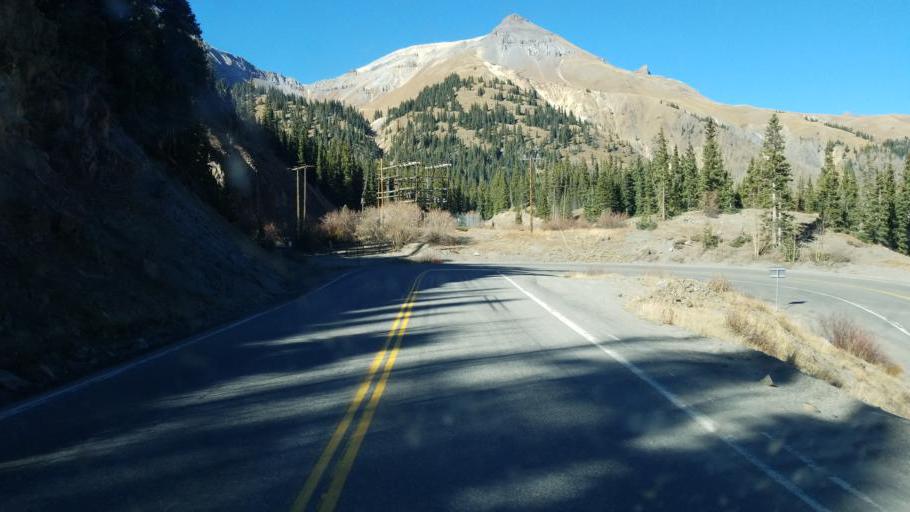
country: US
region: Colorado
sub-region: San Juan County
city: Silverton
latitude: 37.9152
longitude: -107.7032
